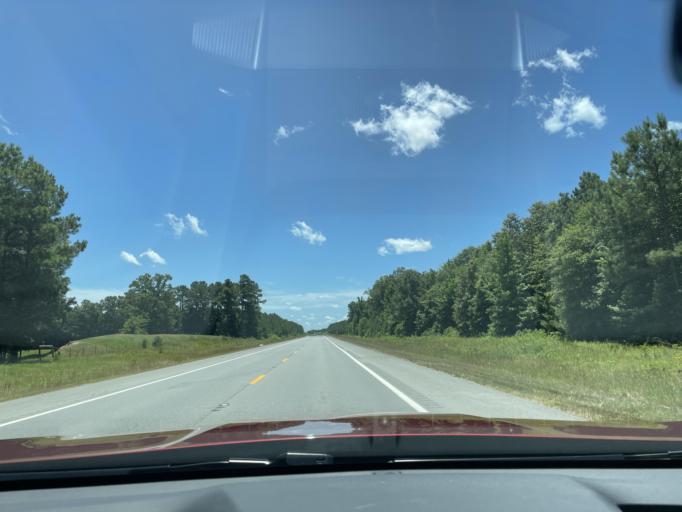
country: US
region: Arkansas
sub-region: Lincoln County
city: Star City
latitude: 33.9682
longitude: -91.9135
